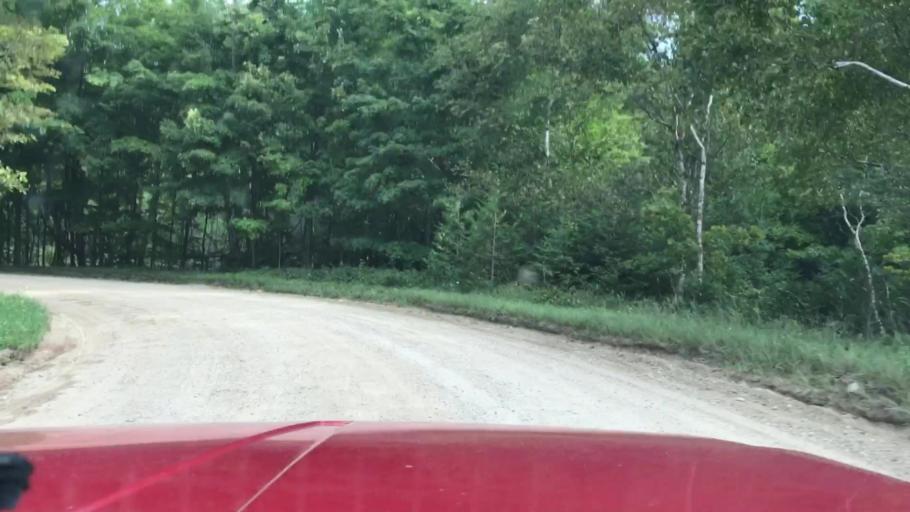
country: US
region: Michigan
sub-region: Charlevoix County
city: Charlevoix
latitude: 45.7417
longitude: -85.5588
